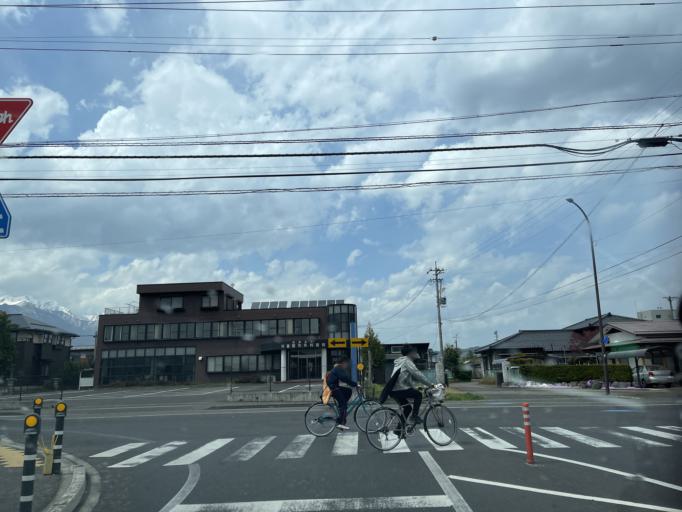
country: JP
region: Nagano
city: Omachi
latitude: 36.5013
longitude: 137.8501
